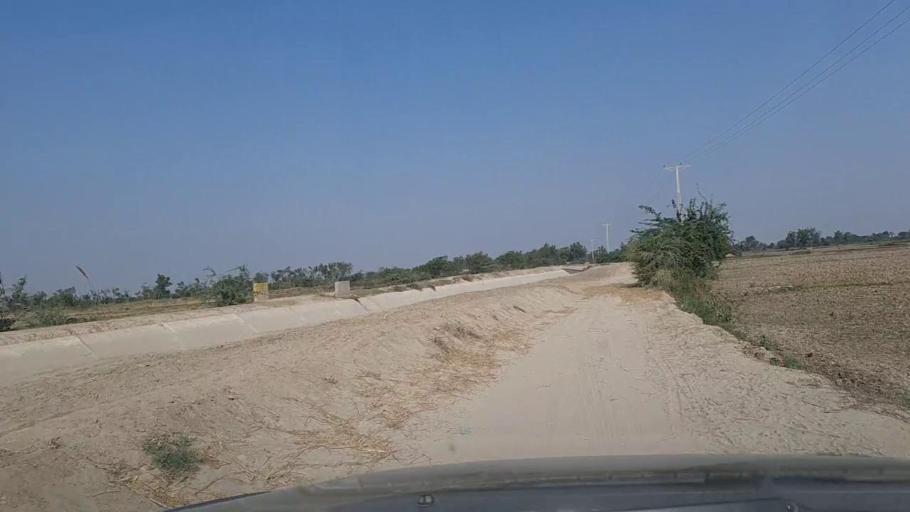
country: PK
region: Sindh
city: Mirpur Sakro
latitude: 24.5147
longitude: 67.8048
